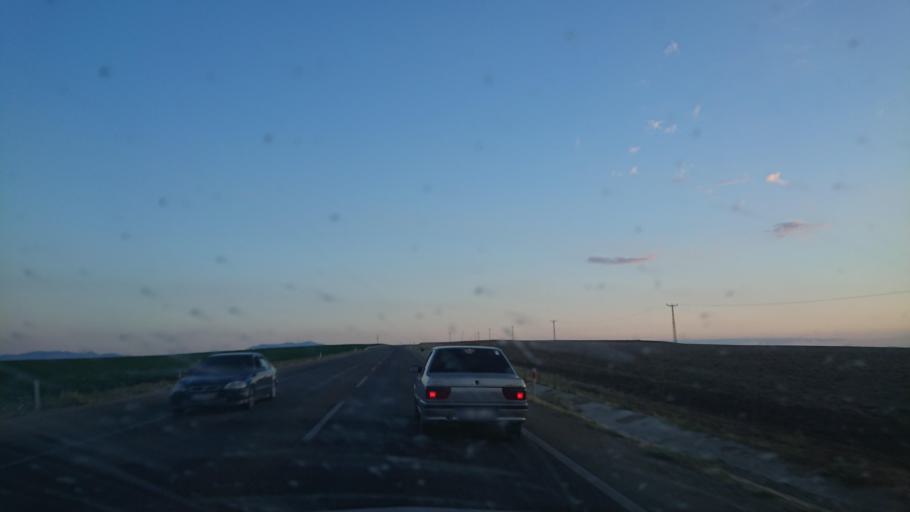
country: TR
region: Aksaray
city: Balci
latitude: 38.9226
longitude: 34.1772
